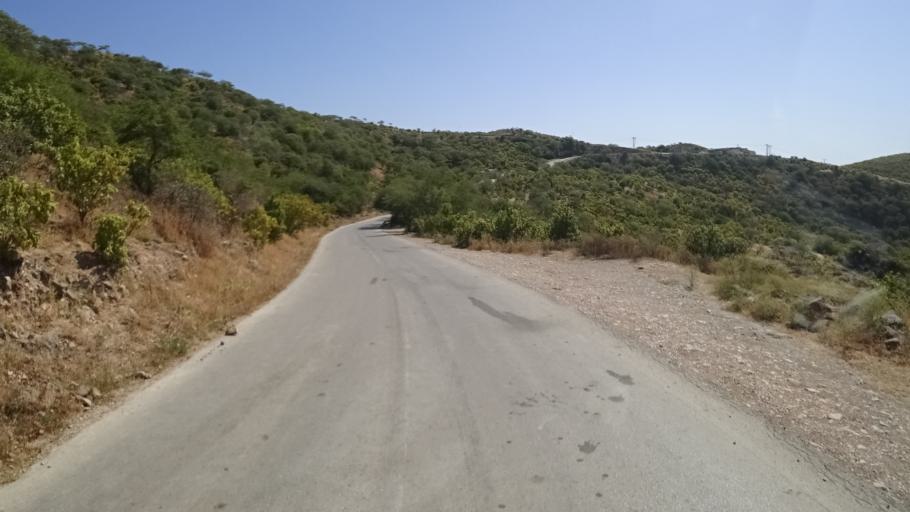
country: OM
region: Zufar
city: Salalah
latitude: 17.0718
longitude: 54.4437
